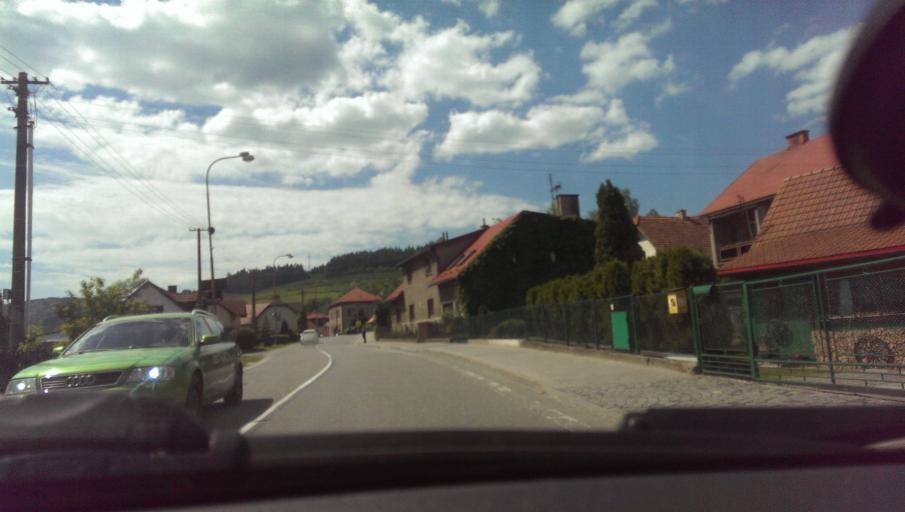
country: CZ
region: Zlin
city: Valasska Polanka
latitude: 49.2613
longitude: 17.9967
